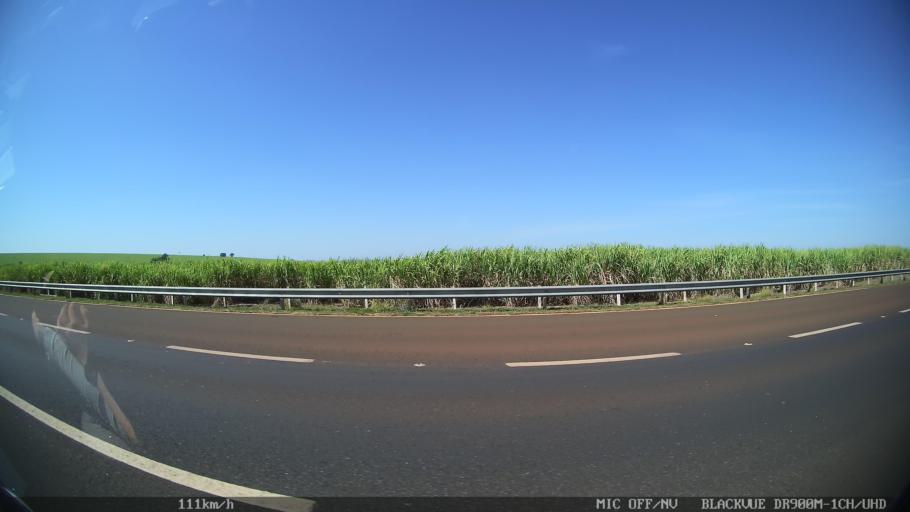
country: BR
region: Sao Paulo
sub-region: Batatais
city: Batatais
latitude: -20.8264
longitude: -47.5944
